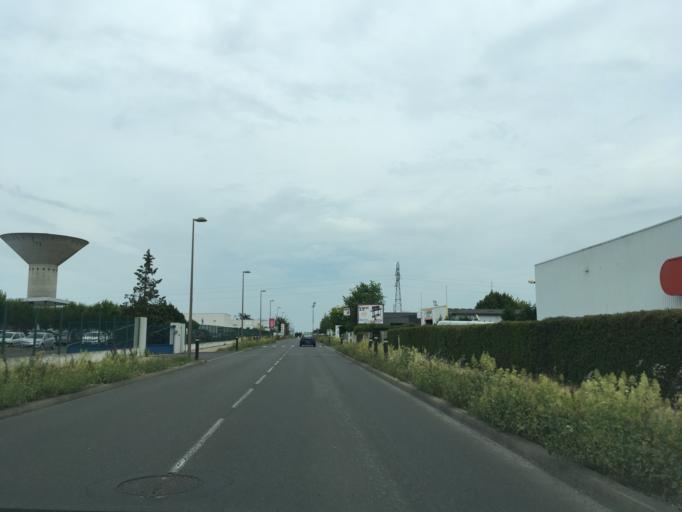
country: FR
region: Poitou-Charentes
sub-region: Departement des Deux-Sevres
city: Bessines
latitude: 46.3146
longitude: -0.4972
